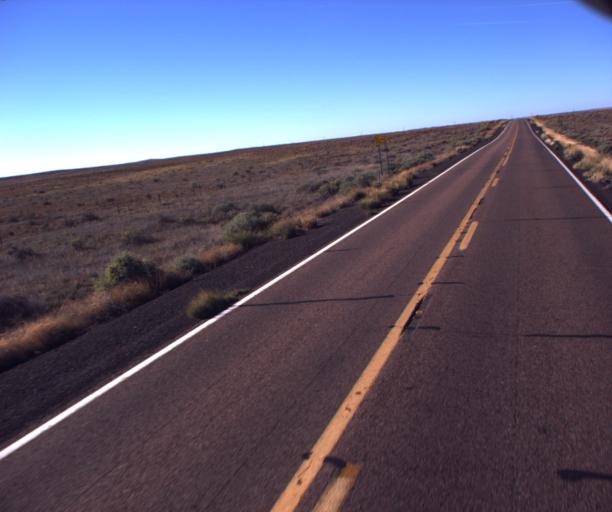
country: US
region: Arizona
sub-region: Navajo County
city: Holbrook
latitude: 34.8283
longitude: -110.1900
